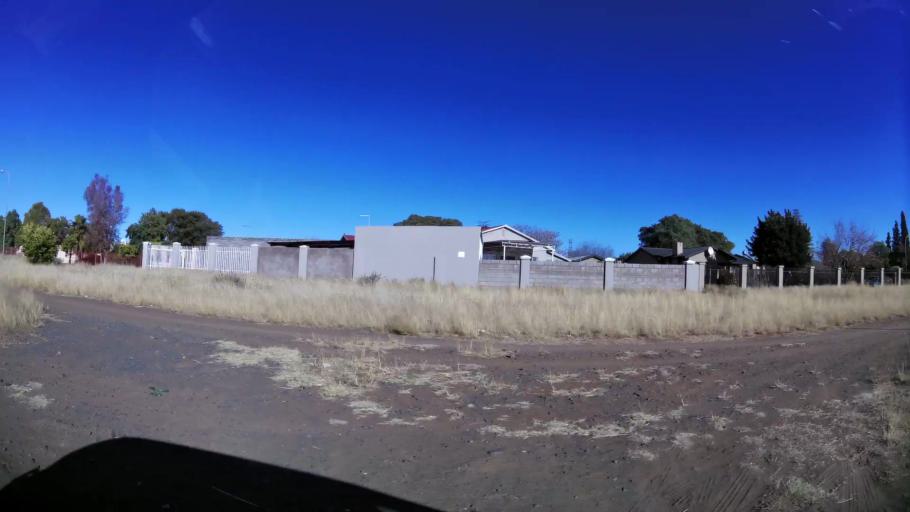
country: ZA
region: Northern Cape
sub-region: Frances Baard District Municipality
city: Kimberley
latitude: -28.7460
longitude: 24.7923
